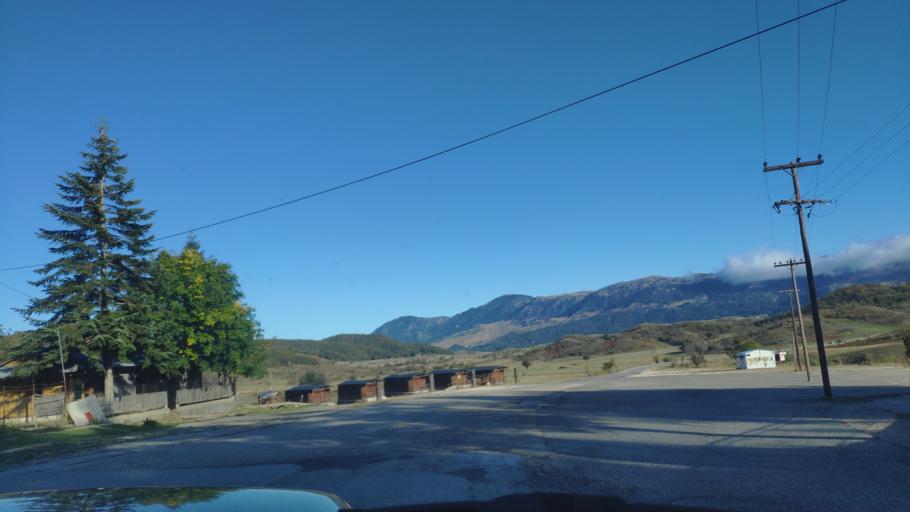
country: GR
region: Epirus
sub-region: Nomos Ioanninon
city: Metsovo
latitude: 39.7843
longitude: 21.1591
